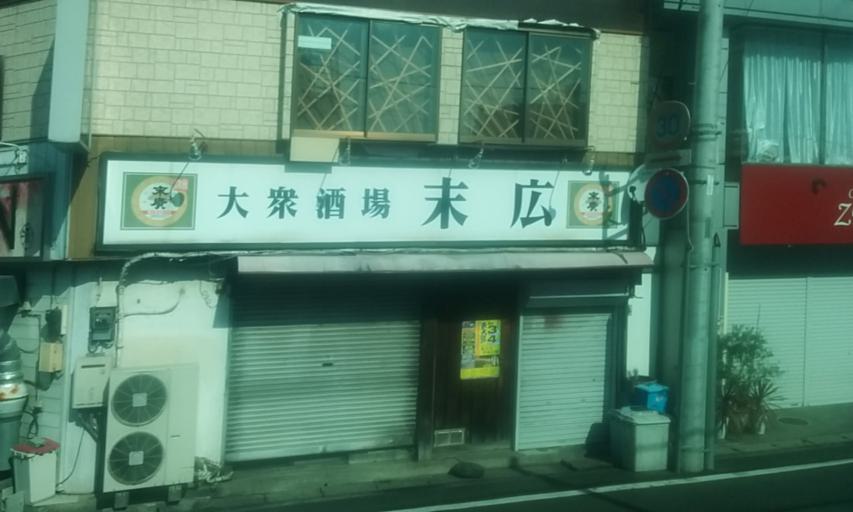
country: JP
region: Saitama
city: Hasuda
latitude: 35.9491
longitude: 139.6404
